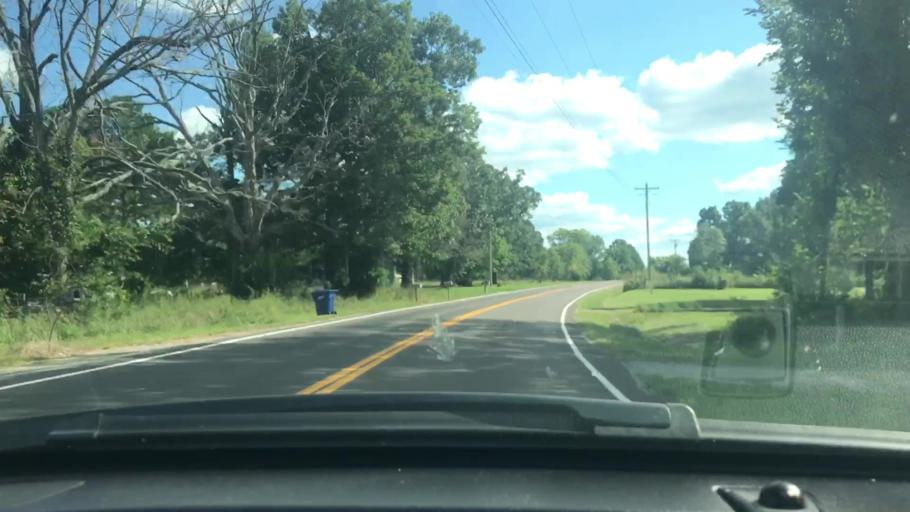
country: US
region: Missouri
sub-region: Wright County
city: Mountain Grove
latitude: 37.2279
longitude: -92.2929
